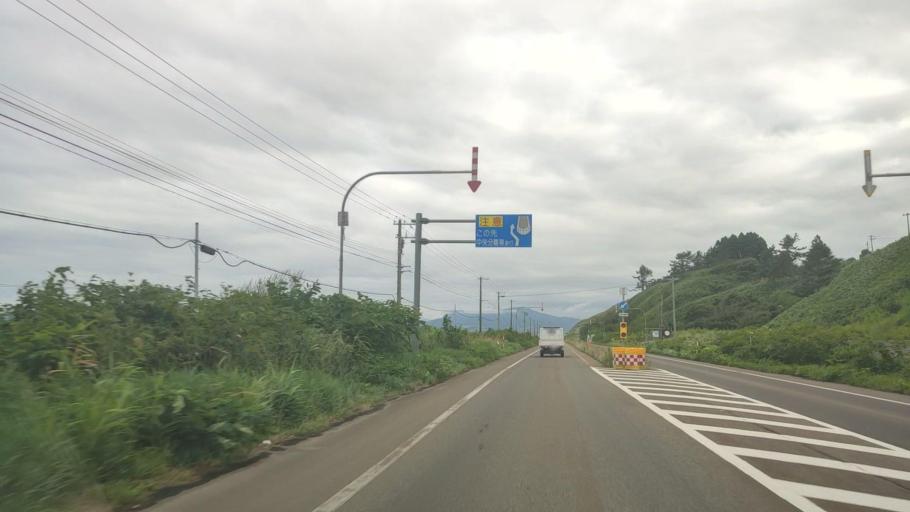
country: JP
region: Hokkaido
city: Niseko Town
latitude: 42.3331
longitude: 140.2785
